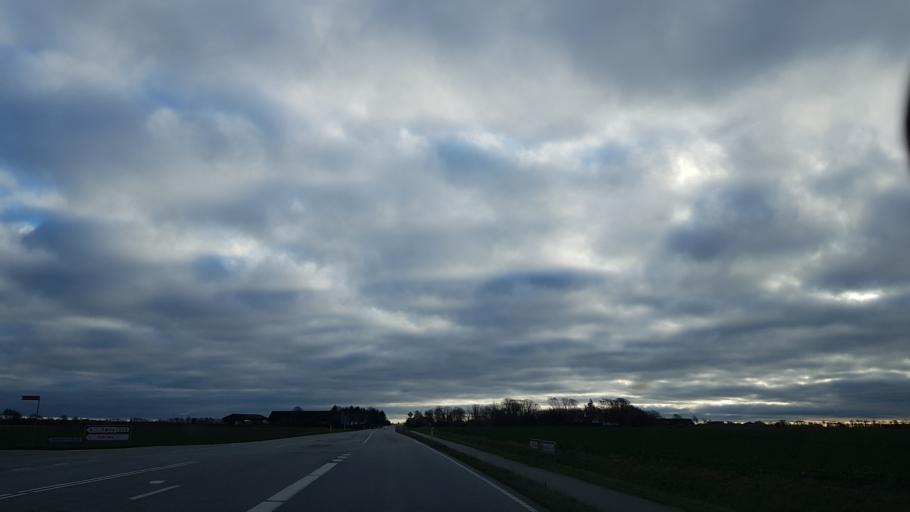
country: DK
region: Zealand
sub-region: Kalundborg Kommune
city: Gorlev
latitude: 55.5272
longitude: 11.2339
